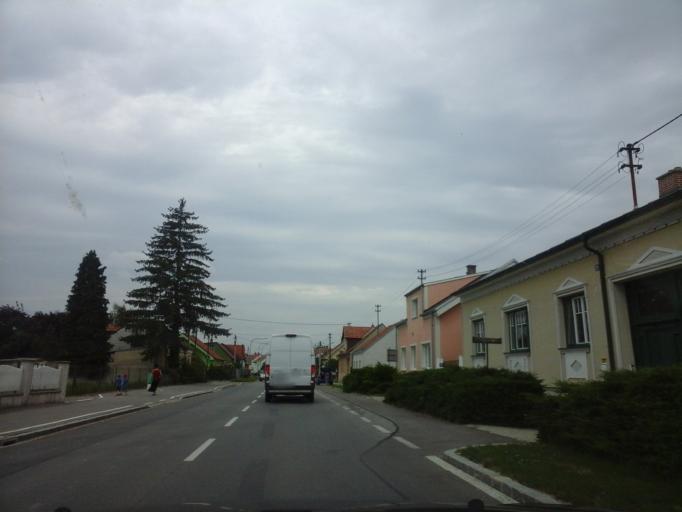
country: AT
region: Lower Austria
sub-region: Politischer Bezirk Ganserndorf
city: Orth an der Donau
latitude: 48.1489
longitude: 16.6949
